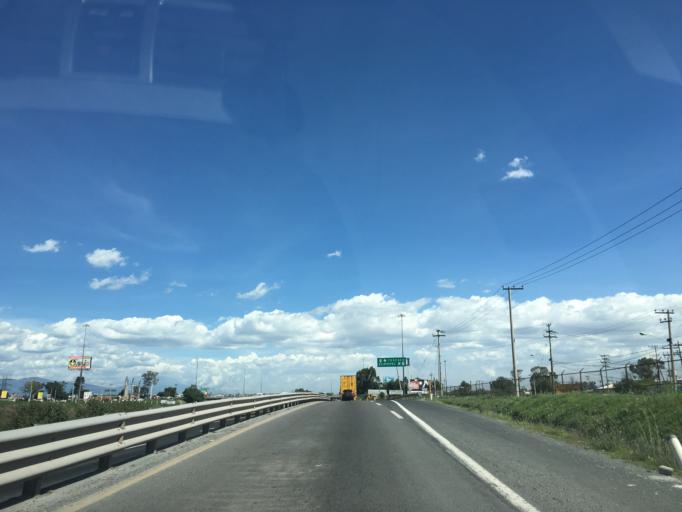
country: MX
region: Mexico
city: Ecatepec
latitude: 19.6170
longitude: -99.0425
